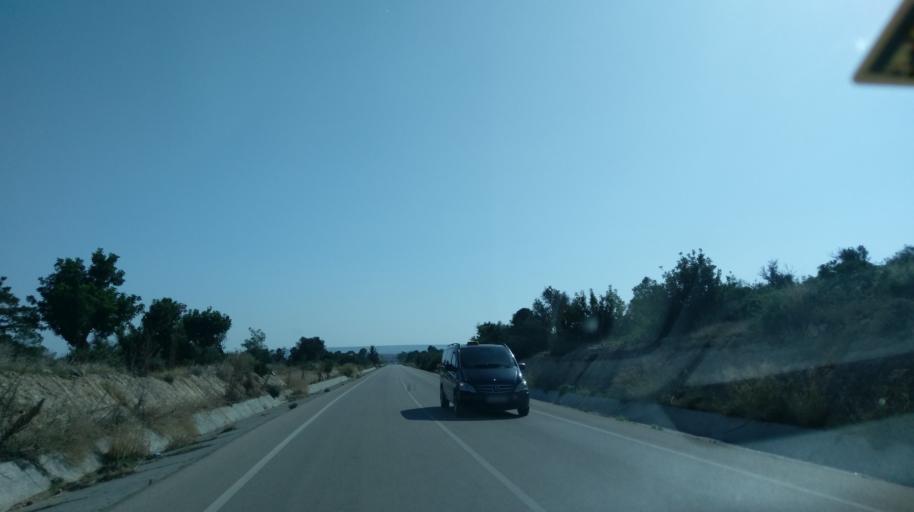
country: CY
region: Ammochostos
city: Trikomo
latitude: 35.4143
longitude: 33.9865
